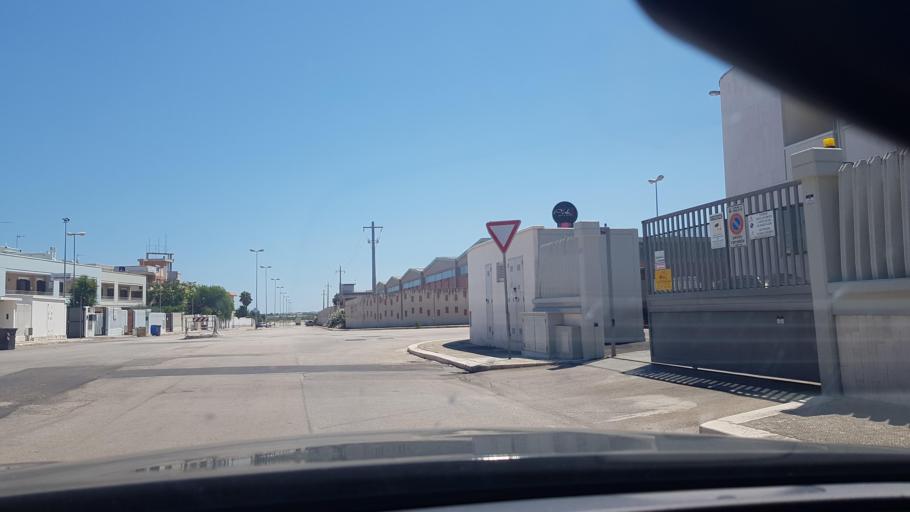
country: IT
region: Apulia
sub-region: Provincia di Barletta - Andria - Trani
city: Barletta
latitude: 41.3048
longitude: 16.3259
